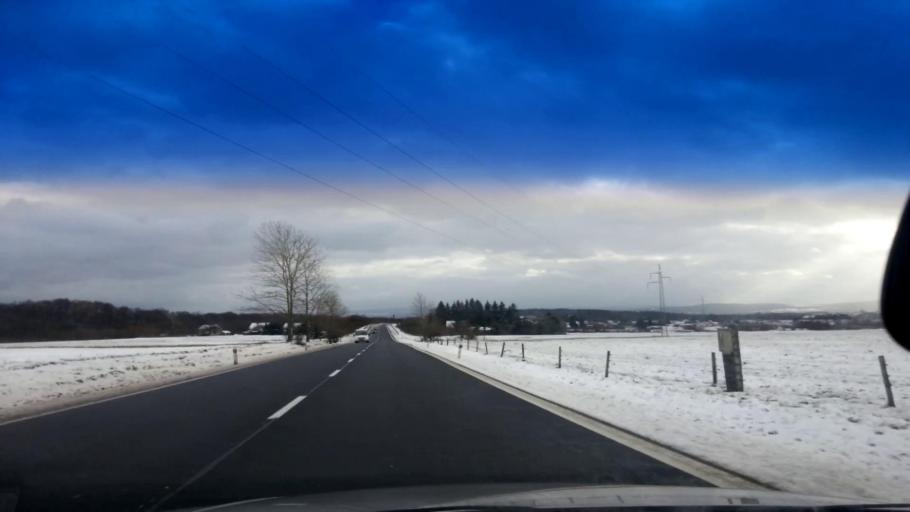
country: CZ
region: Karlovarsky
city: Hazlov
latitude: 50.1686
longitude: 12.2643
